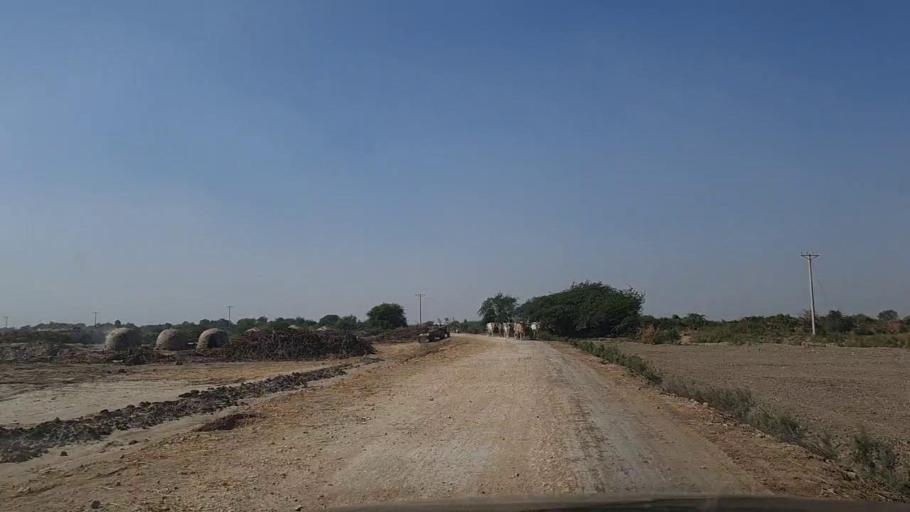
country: PK
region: Sindh
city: Daro Mehar
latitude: 24.8346
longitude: 68.1844
